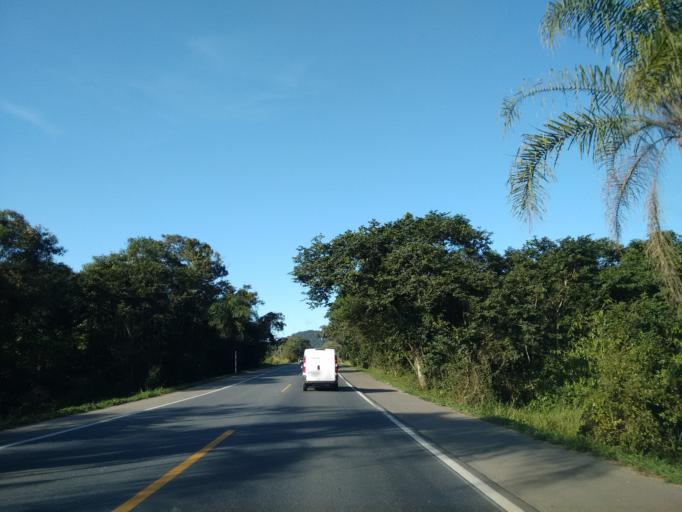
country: BR
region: Santa Catarina
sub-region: Joinville
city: Joinville
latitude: -26.4488
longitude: -48.8376
